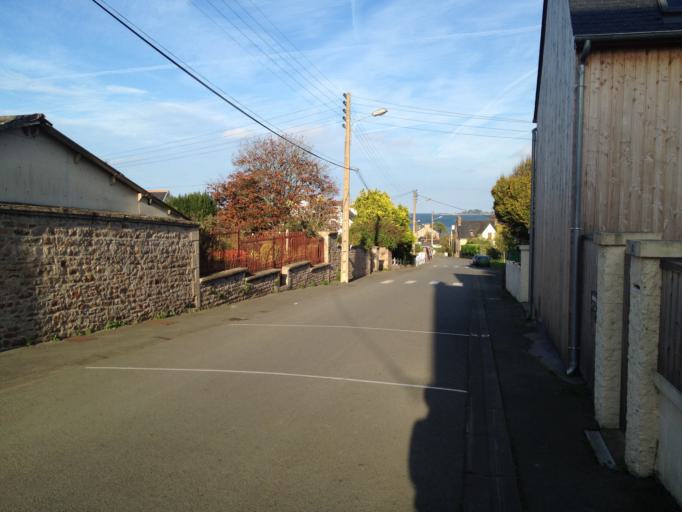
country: FR
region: Brittany
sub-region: Departement des Cotes-d'Armor
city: Paimpol
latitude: 48.7688
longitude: -3.0238
